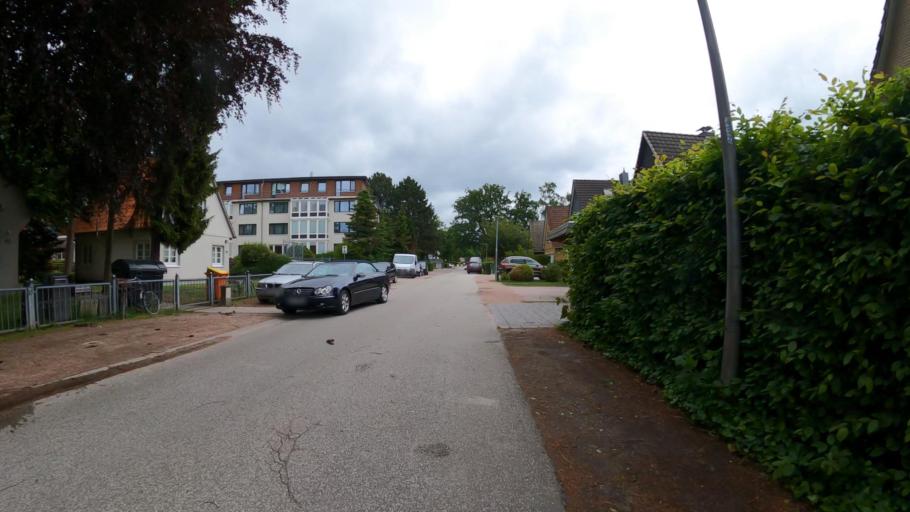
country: DE
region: Schleswig-Holstein
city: Norderstedt
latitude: 53.7050
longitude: 9.9973
